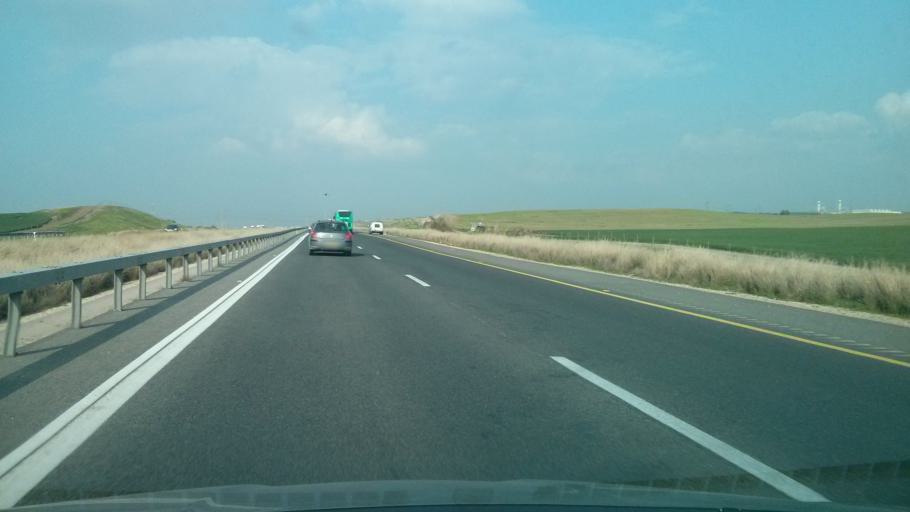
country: IL
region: Southern District
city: Qiryat Gat
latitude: 31.7006
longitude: 34.8172
